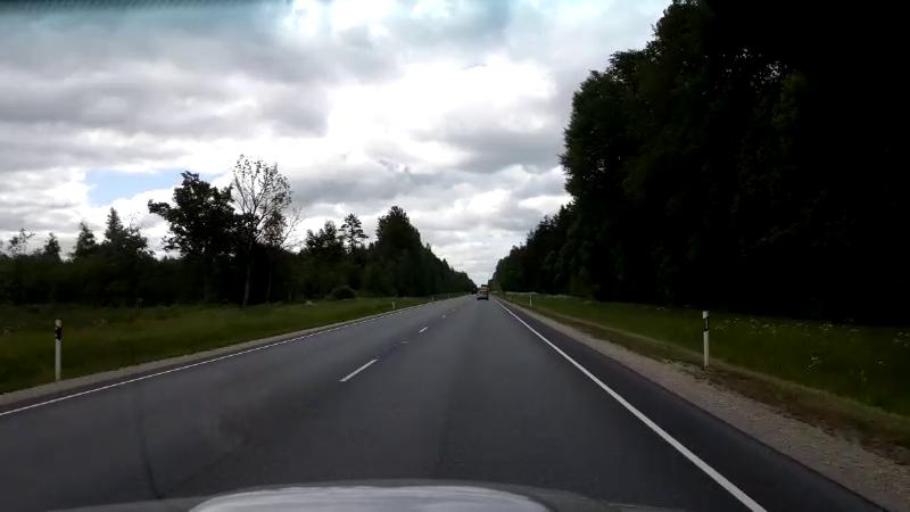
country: EE
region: Raplamaa
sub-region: Maerjamaa vald
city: Marjamaa
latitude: 58.7970
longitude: 24.4128
